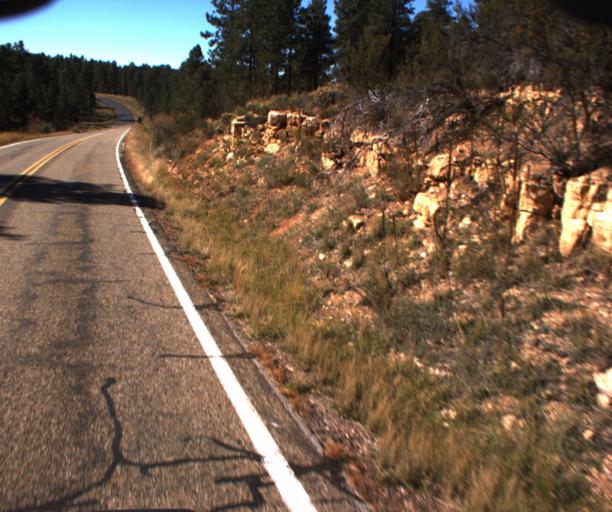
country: US
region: Arizona
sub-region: Coconino County
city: Fredonia
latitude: 36.7587
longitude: -112.2663
